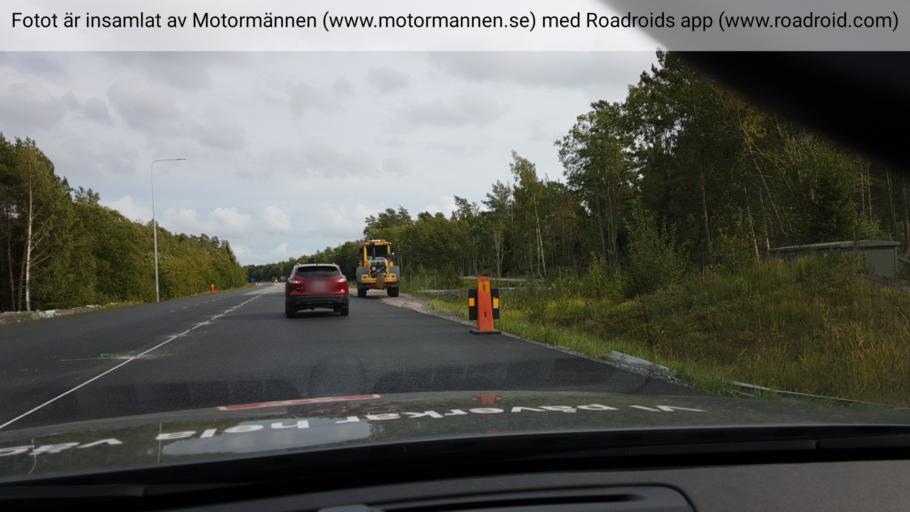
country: SE
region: Stockholm
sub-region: Norrtalje Kommun
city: Bjorko
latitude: 59.7204
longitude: 18.9569
